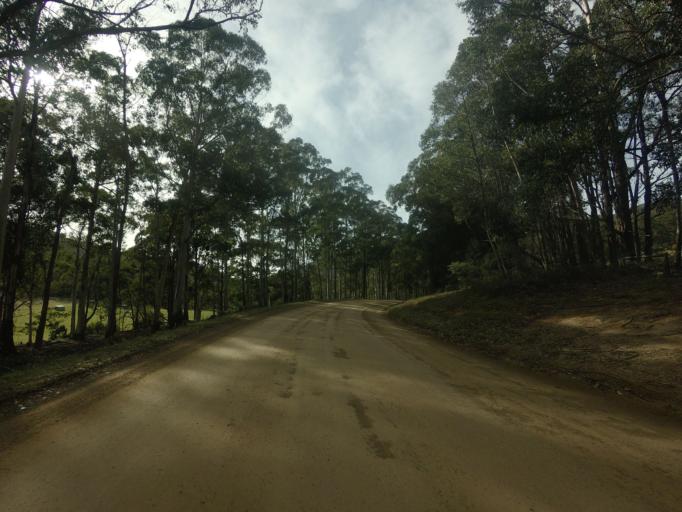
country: AU
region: Tasmania
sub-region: Huon Valley
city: Huonville
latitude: -43.0736
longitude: 147.0769
